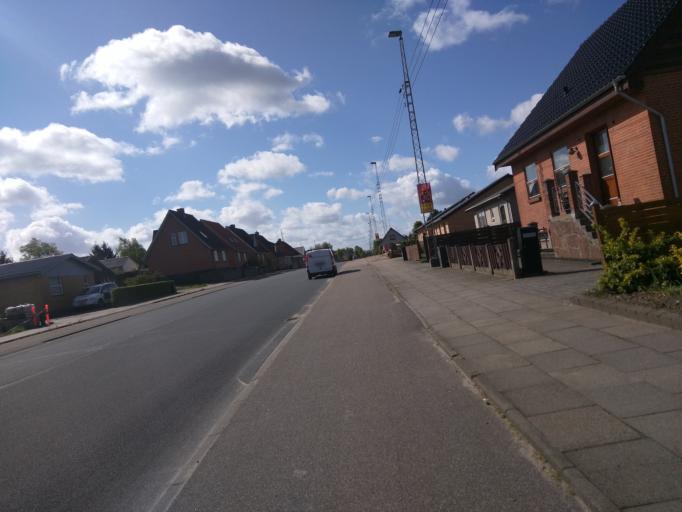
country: DK
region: Central Jutland
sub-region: Viborg Kommune
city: Viborg
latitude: 56.4299
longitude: 9.4021
